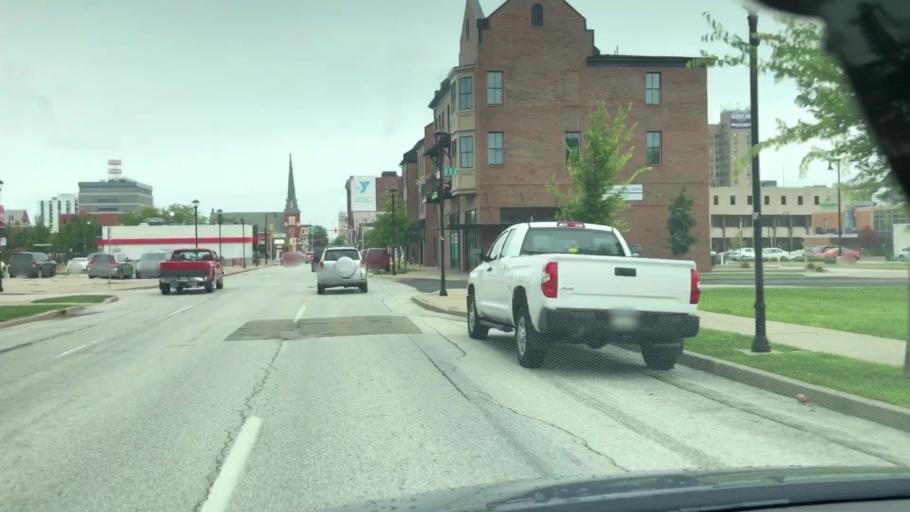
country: US
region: Pennsylvania
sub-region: Erie County
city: Erie
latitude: 42.1219
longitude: -80.0819
